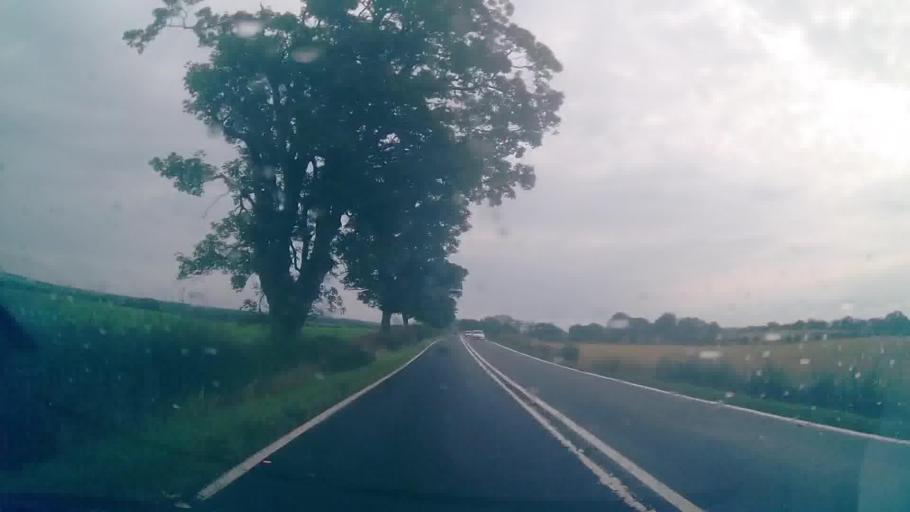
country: GB
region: Scotland
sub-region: Dumfries and Galloway
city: Lochmaben
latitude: 55.0642
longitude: -3.5011
